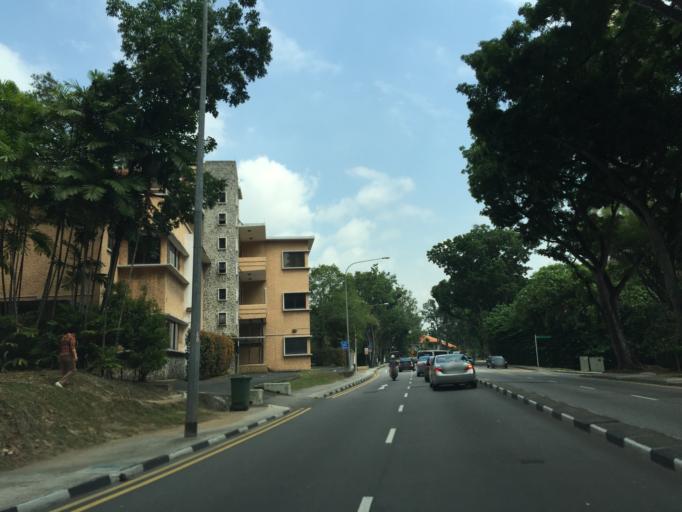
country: SG
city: Singapore
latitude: 1.2998
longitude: 103.8251
